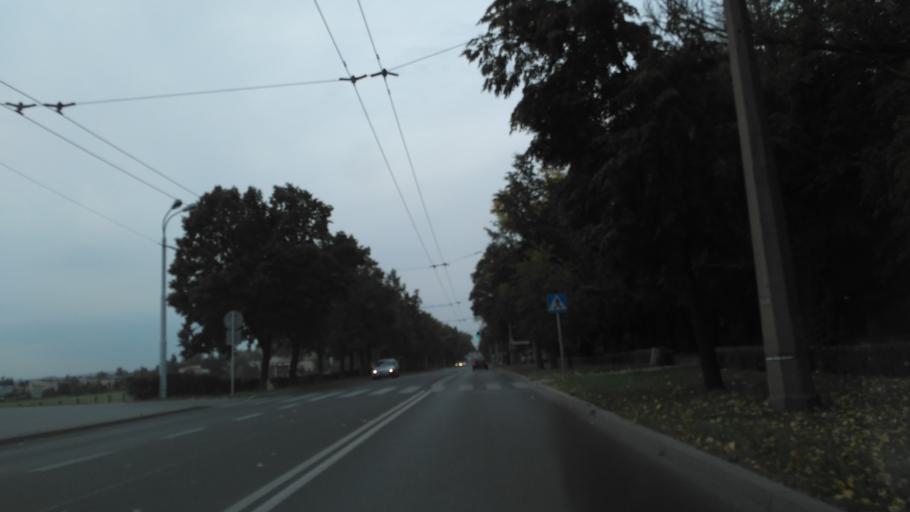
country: PL
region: Lublin Voivodeship
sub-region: Powiat lubelski
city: Lublin
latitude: 51.2262
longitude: 22.6054
